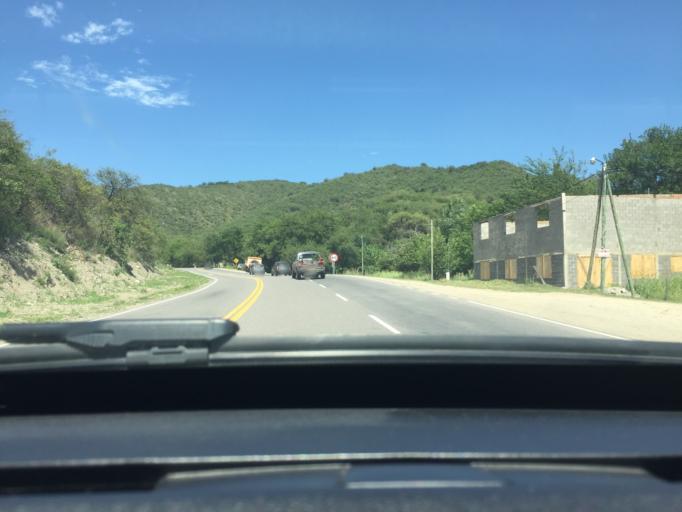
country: AR
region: Cordoba
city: Alta Gracia
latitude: -31.7417
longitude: -64.4613
